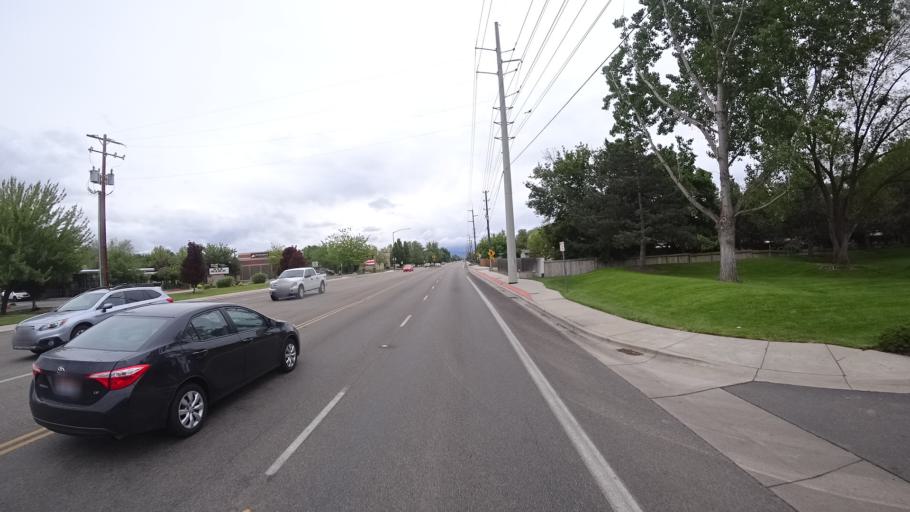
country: US
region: Idaho
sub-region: Ada County
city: Eagle
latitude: 43.6339
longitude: -116.3132
